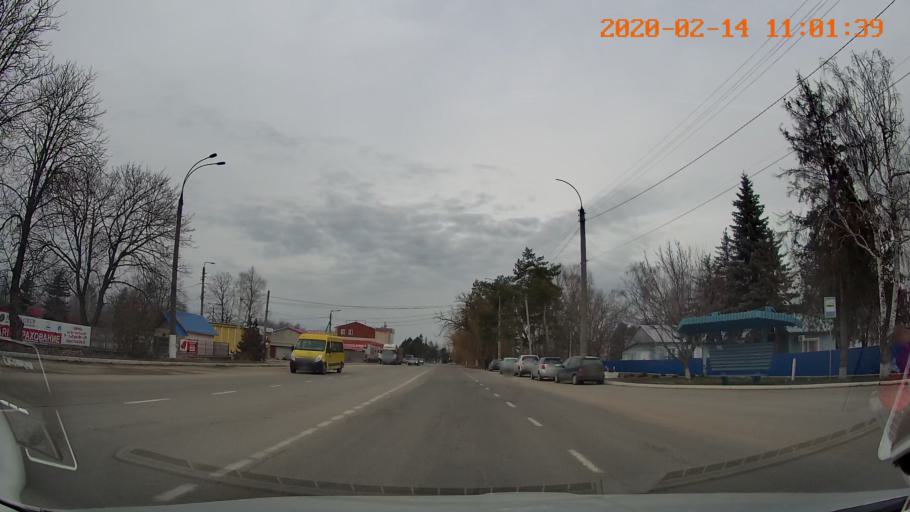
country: MD
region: Raionul Edinet
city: Edinet
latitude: 48.1611
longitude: 27.3273
